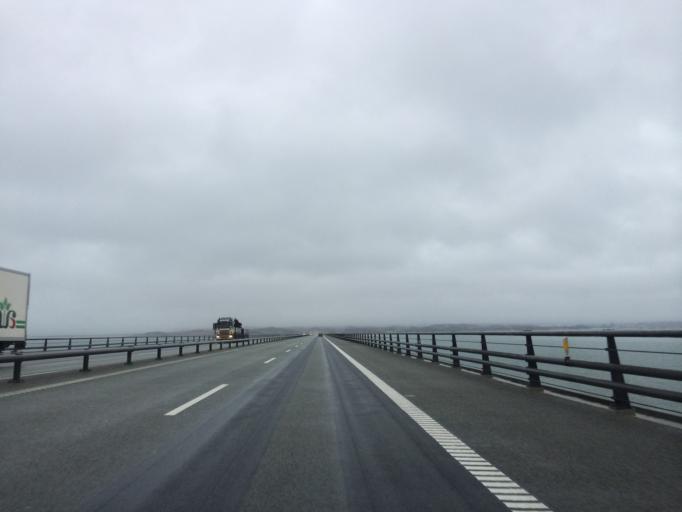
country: DK
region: Zealand
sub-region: Slagelse Kommune
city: Korsor
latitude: 55.3447
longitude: 11.0576
